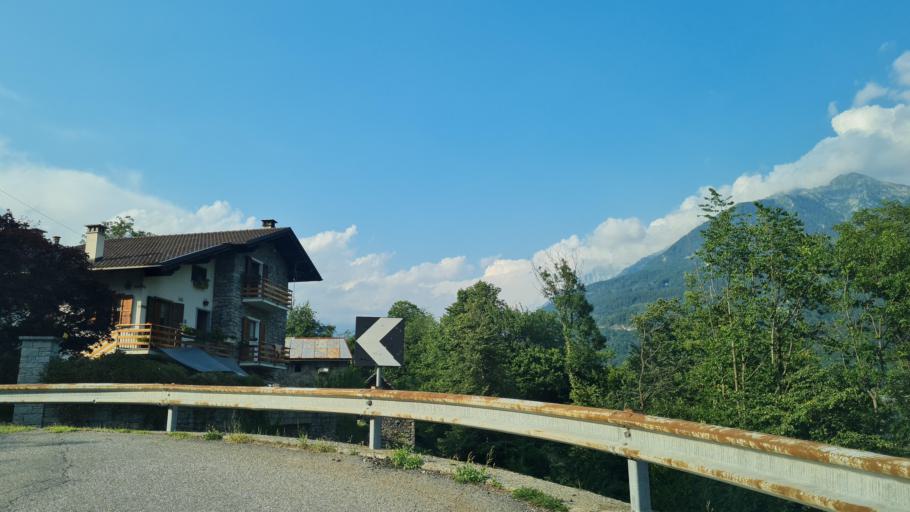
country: IT
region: Piedmont
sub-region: Provincia Verbano-Cusio-Ossola
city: Crodo
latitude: 46.2223
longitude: 8.3179
